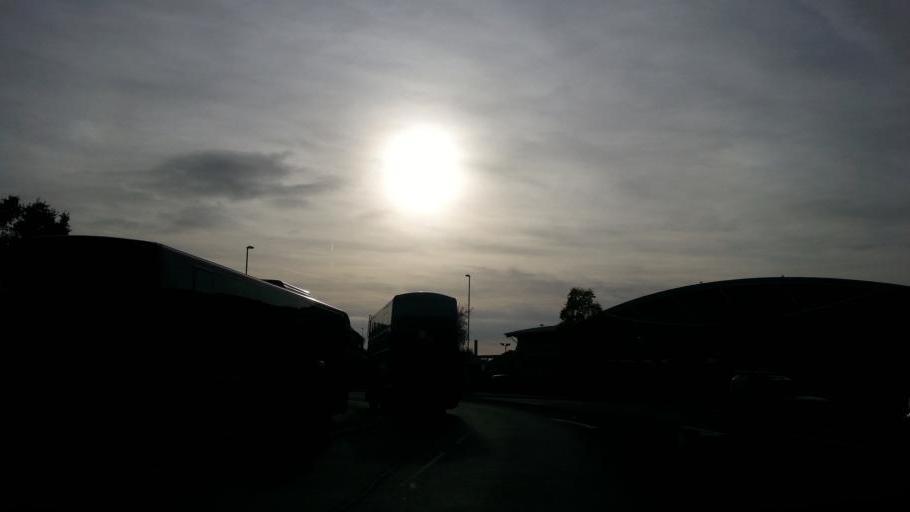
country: GB
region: England
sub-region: Northamptonshire
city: Northampton
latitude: 52.2368
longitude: -0.9115
